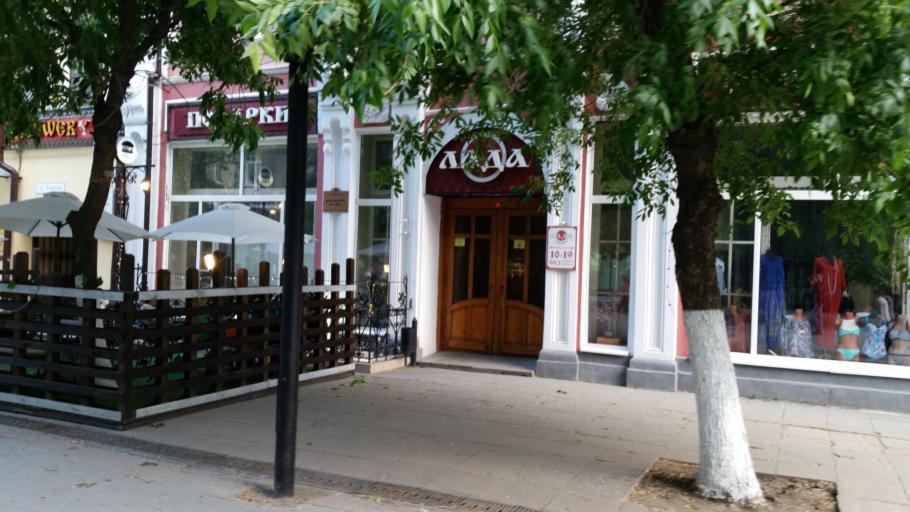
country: RU
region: Saratov
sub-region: Saratovskiy Rayon
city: Saratov
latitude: 51.5304
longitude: 46.0328
